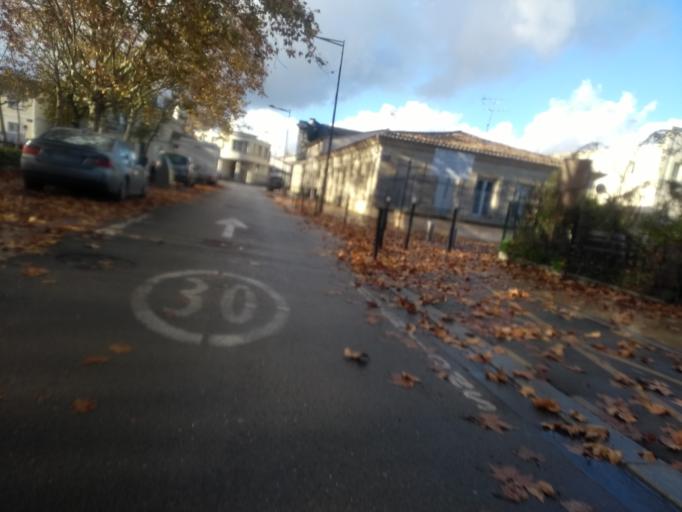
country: FR
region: Aquitaine
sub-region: Departement de la Gironde
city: Begles
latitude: 44.8242
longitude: -0.5509
